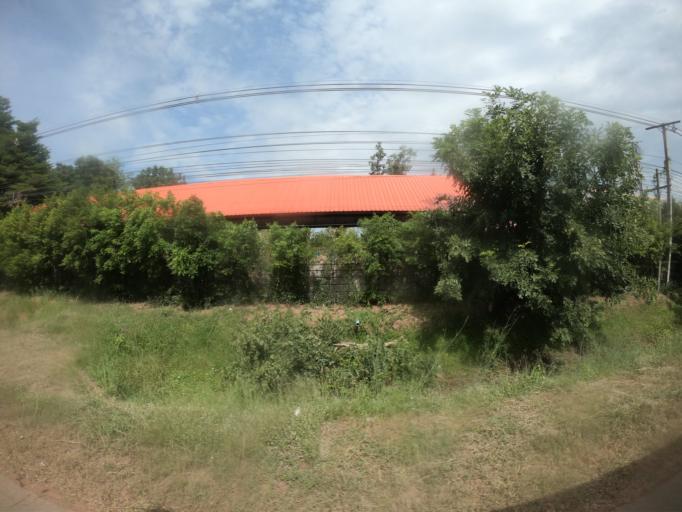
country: TH
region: Maha Sarakham
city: Chiang Yuen
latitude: 16.3434
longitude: 103.1375
